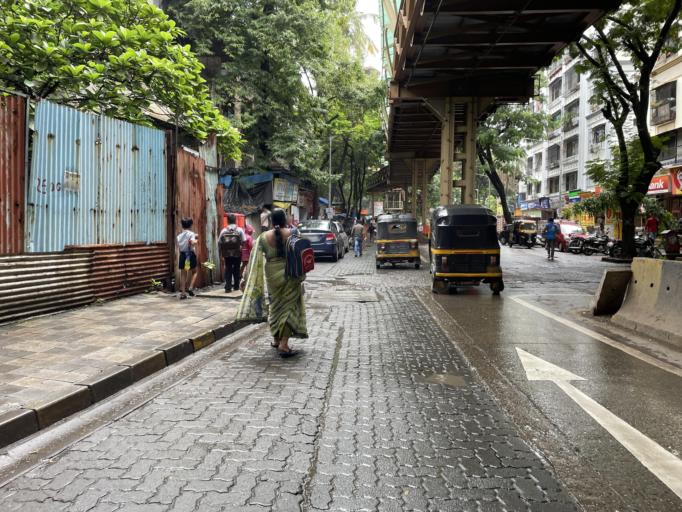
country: IN
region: Maharashtra
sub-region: Mumbai Suburban
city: Borivli
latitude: 19.2538
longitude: 72.8582
